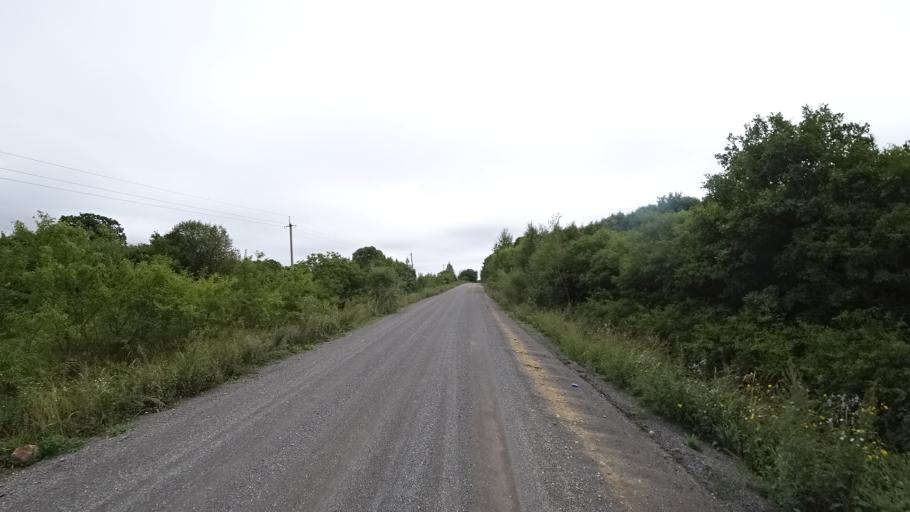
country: RU
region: Primorskiy
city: Lyalichi
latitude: 44.0719
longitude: 132.4765
